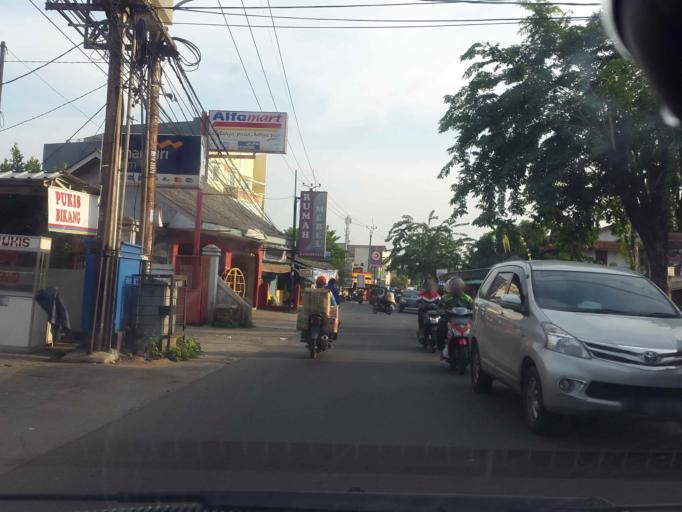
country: ID
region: West Java
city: Ciputat
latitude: -6.2559
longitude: 106.7041
